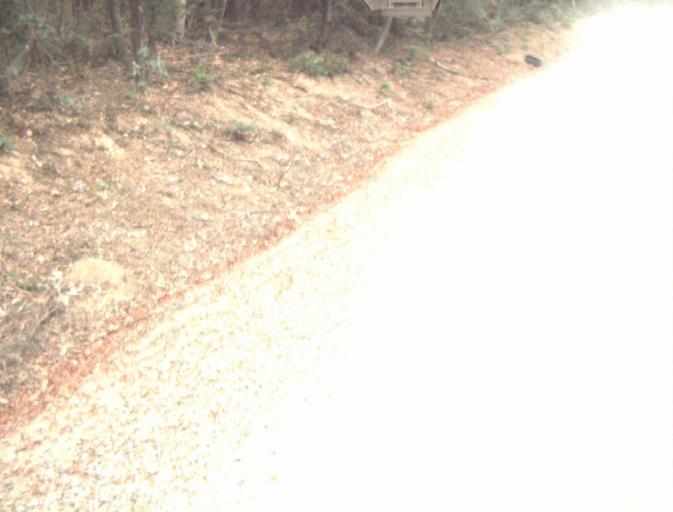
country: AU
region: Tasmania
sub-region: Northern Midlands
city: Evandale
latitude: -41.4613
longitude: 147.4958
